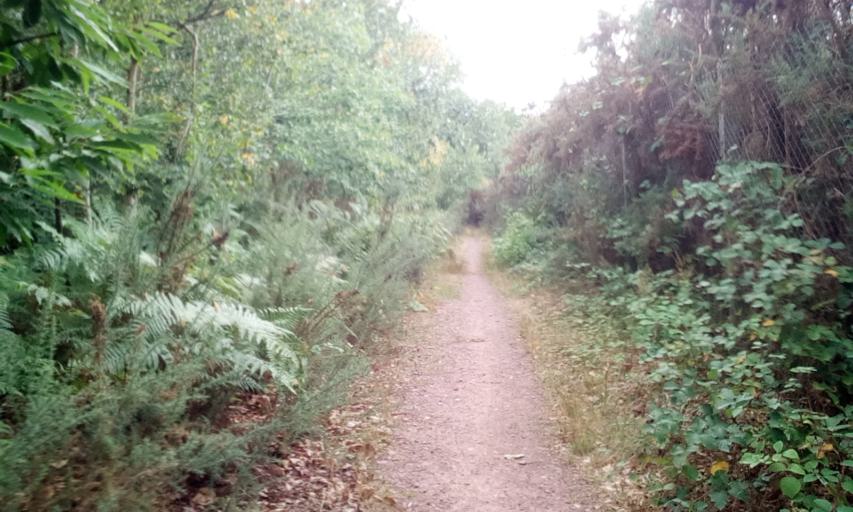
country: FR
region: Lower Normandy
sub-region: Departement du Calvados
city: Mouen
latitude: 49.1374
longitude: -0.4814
